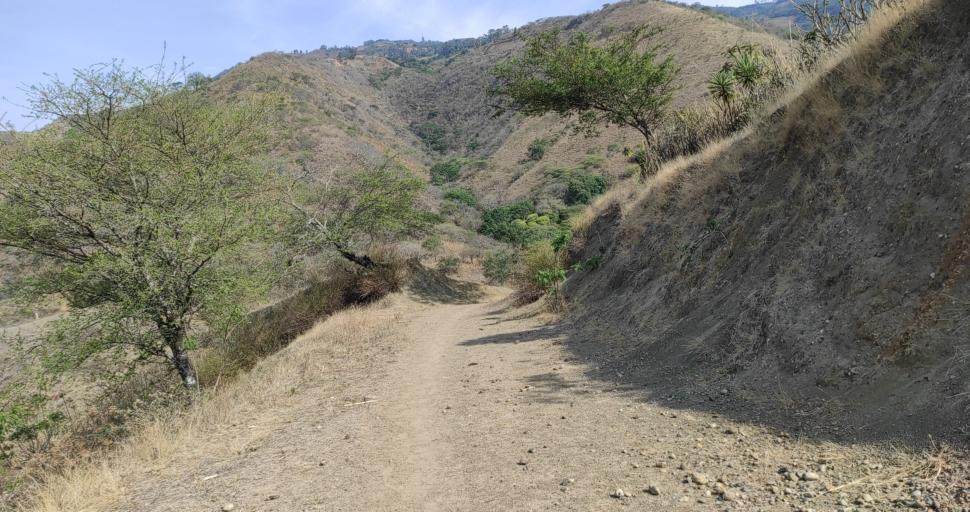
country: EC
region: Loja
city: Catacocha
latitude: -4.0008
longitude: -79.7145
